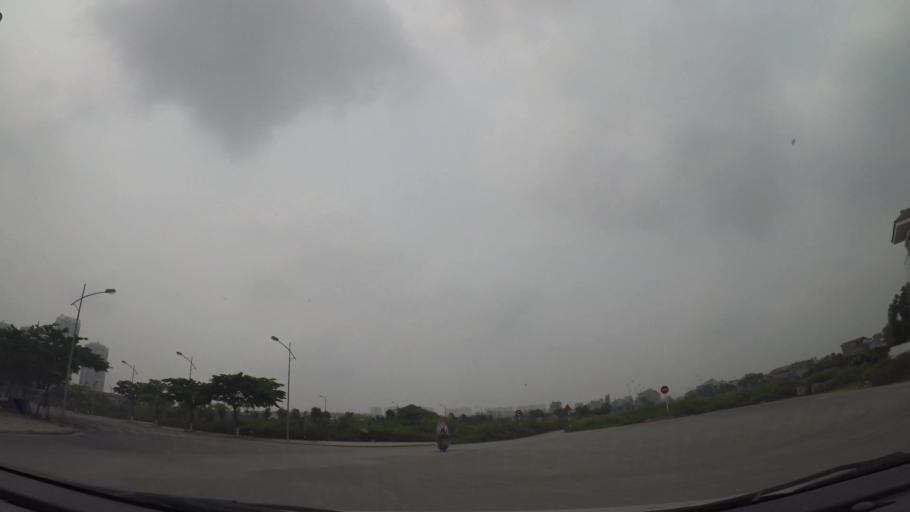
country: VN
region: Ha Noi
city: Ha Dong
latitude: 20.9797
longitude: 105.7530
